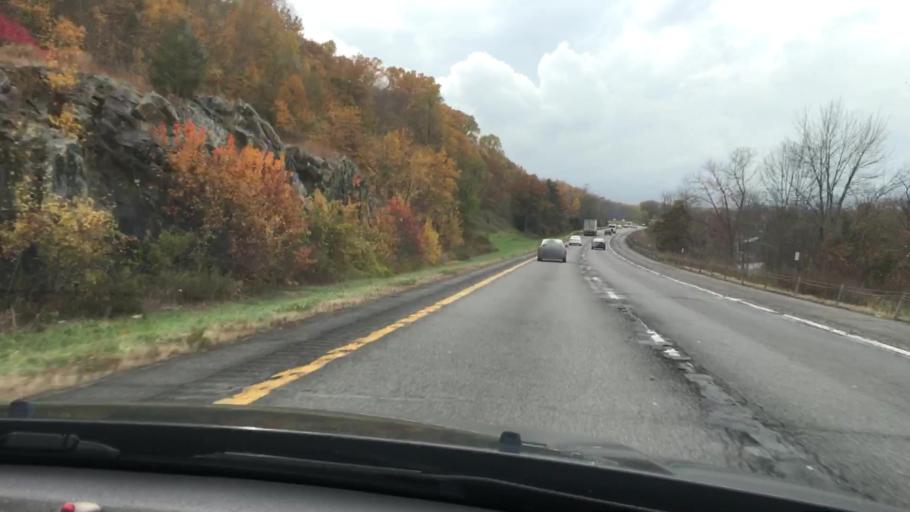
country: US
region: New York
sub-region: Dutchess County
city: Hillside Lake
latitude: 41.5419
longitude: -73.7585
